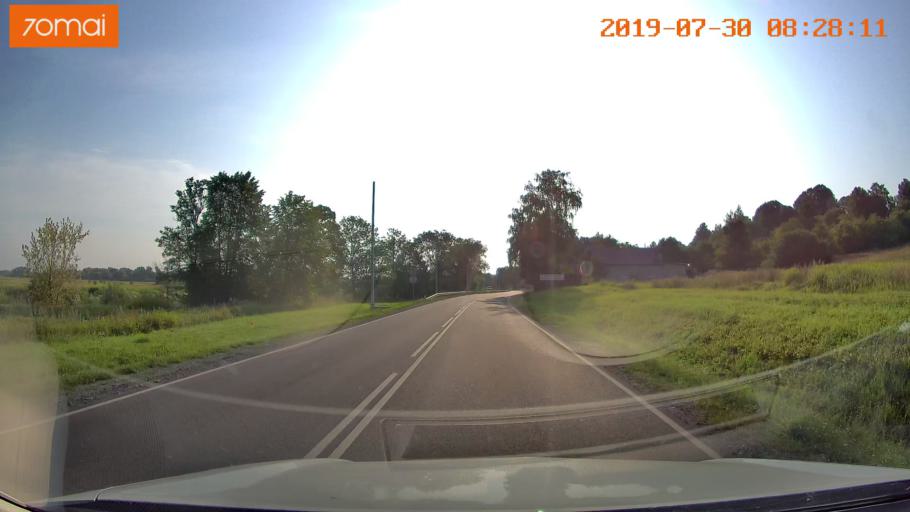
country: RU
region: Kaliningrad
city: Chernyakhovsk
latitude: 54.6291
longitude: 21.6414
